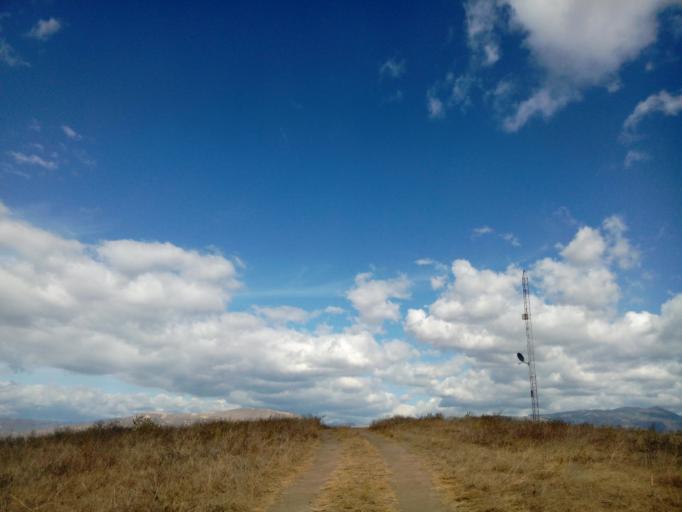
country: EC
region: Imbabura
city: Atuntaqui
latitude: 0.4178
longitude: -78.1852
